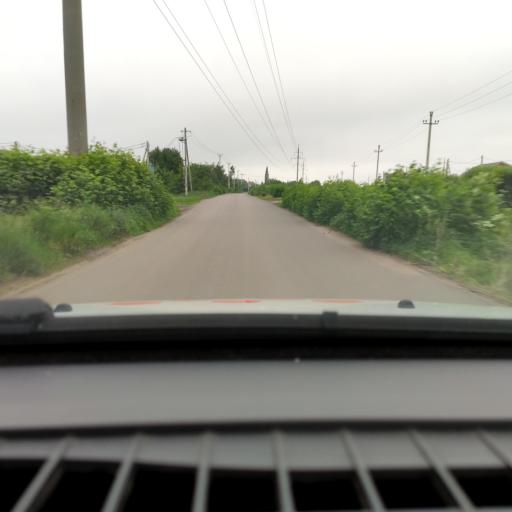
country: RU
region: Voronezj
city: Novaya Usman'
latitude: 51.6588
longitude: 39.4077
